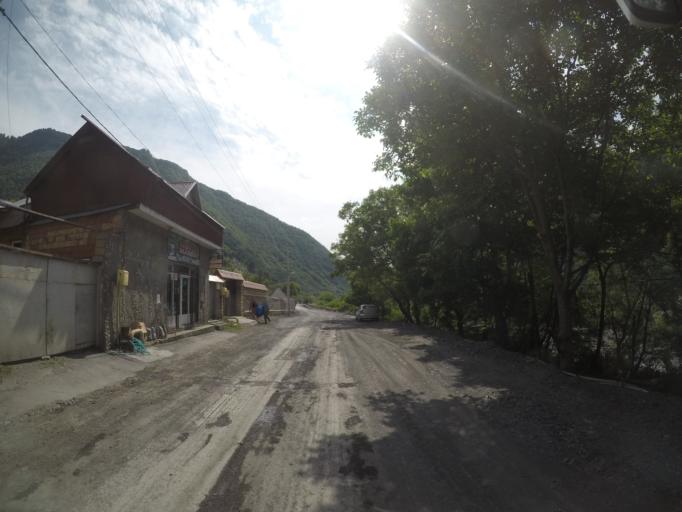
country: AZ
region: Qakh Rayon
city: Qaxbas
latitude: 41.4675
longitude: 47.0516
